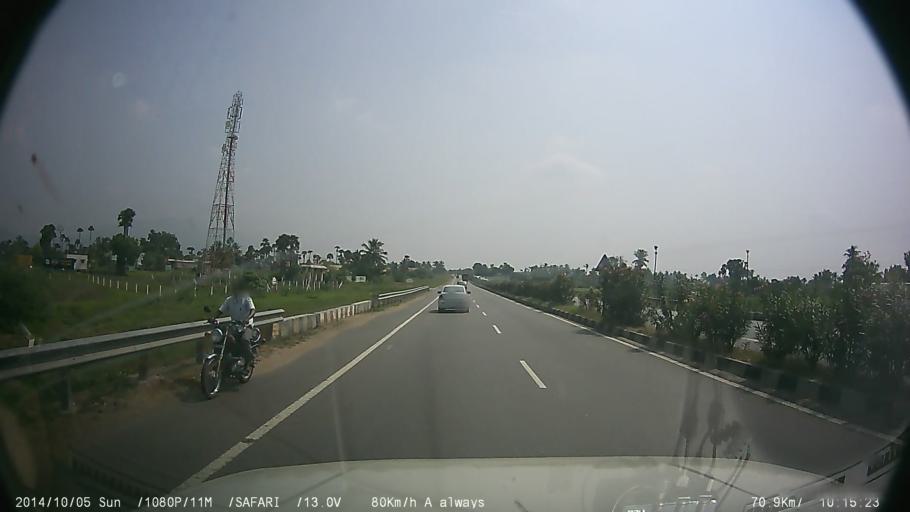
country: IN
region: Tamil Nadu
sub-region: Salem
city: Attayyampatti
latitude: 11.5606
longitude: 78.0190
